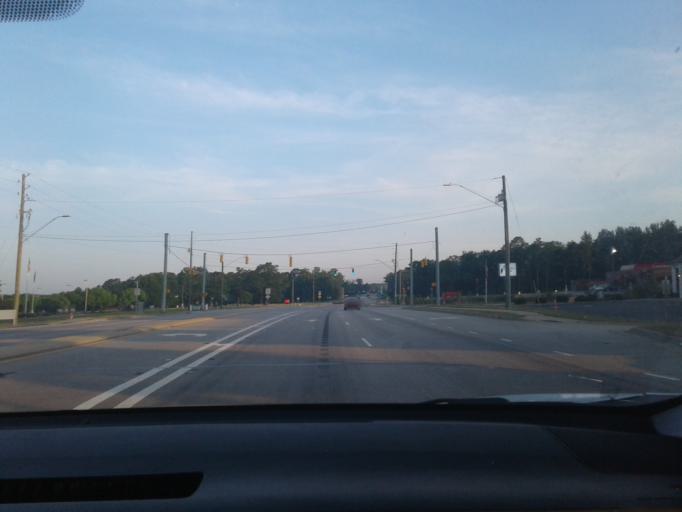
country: US
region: North Carolina
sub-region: Harnett County
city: Lillington
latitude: 35.4195
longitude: -78.8064
